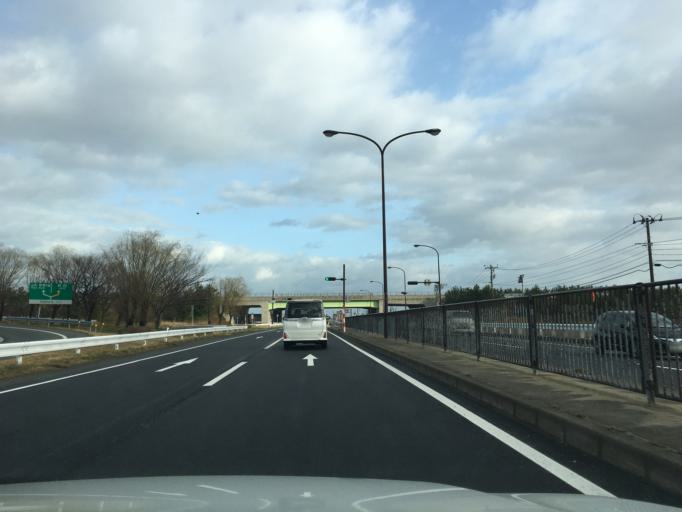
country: JP
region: Yamagata
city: Sakata
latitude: 38.8678
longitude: 139.8423
